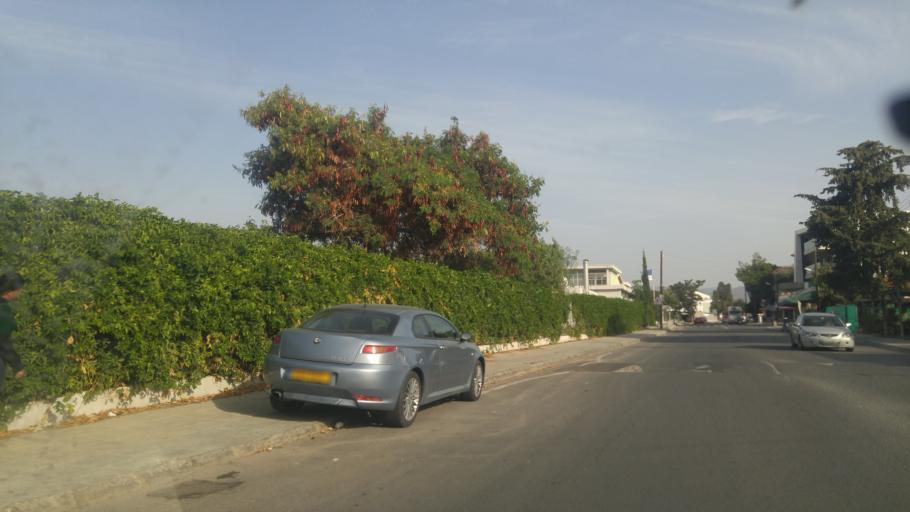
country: CY
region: Limassol
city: Limassol
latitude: 34.6729
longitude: 33.0063
